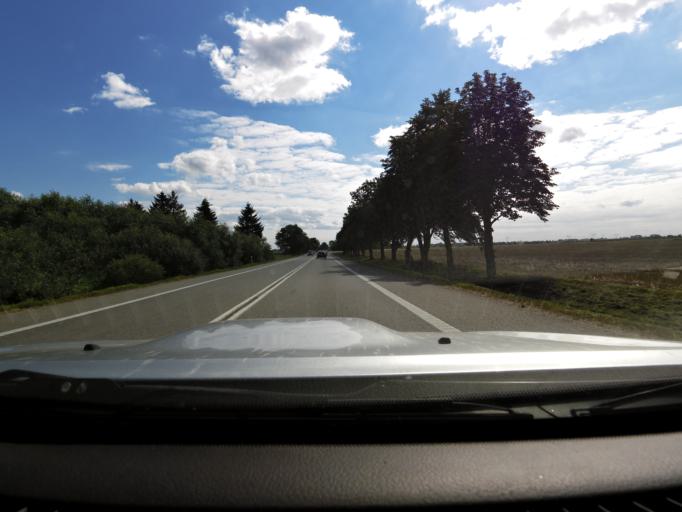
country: PL
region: Pomeranian Voivodeship
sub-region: Powiat nowodworski
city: Nowy Dwor Gdanski
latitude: 54.1838
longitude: 19.2183
